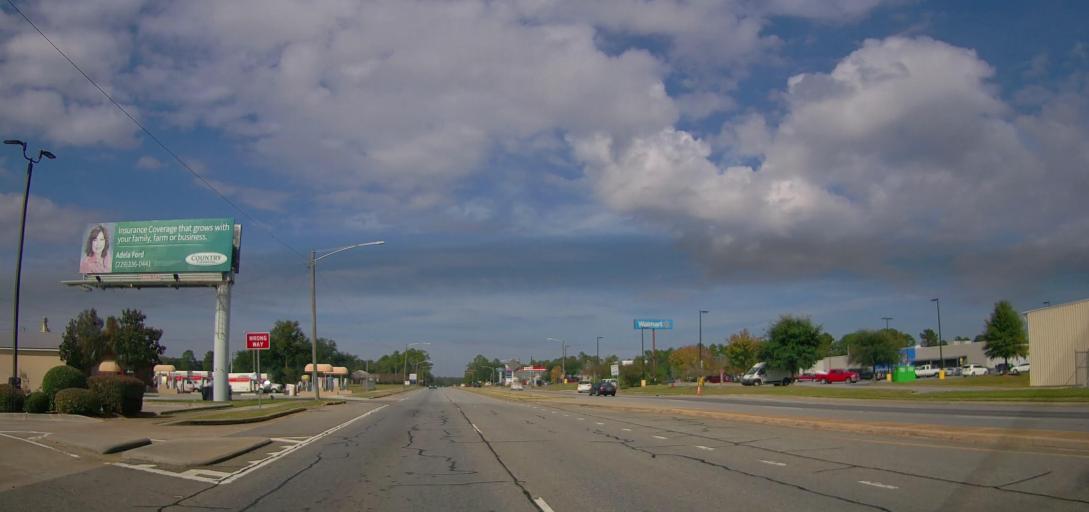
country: US
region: Georgia
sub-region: Mitchell County
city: Camilla
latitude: 31.2344
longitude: -84.2001
